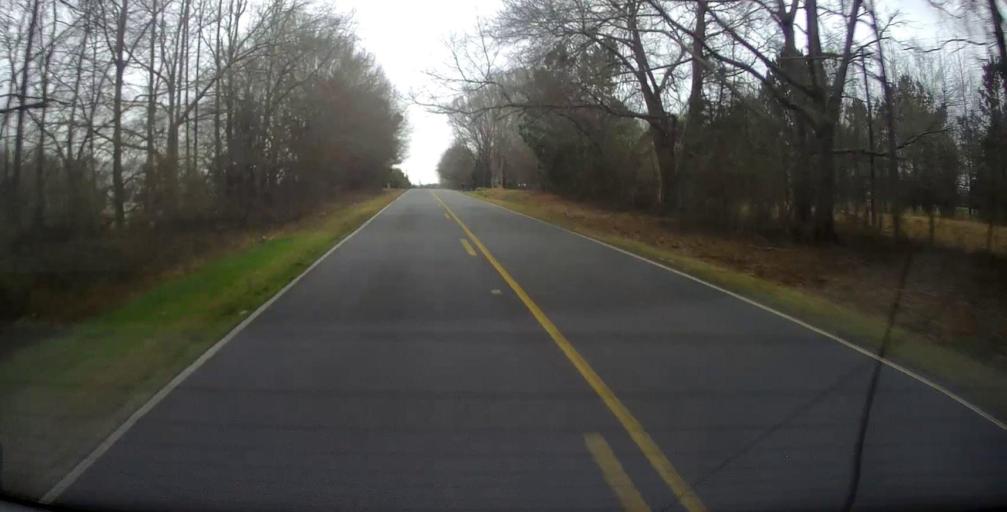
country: US
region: Georgia
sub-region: Pike County
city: Zebulon
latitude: 33.0595
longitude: -84.3245
